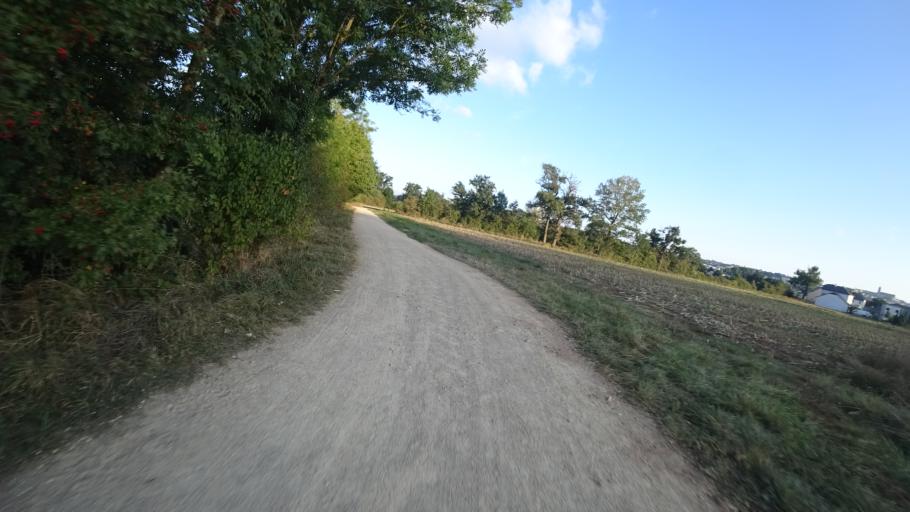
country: FR
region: Midi-Pyrenees
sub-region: Departement de l'Aveyron
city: Rodez
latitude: 44.3793
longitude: 2.5828
